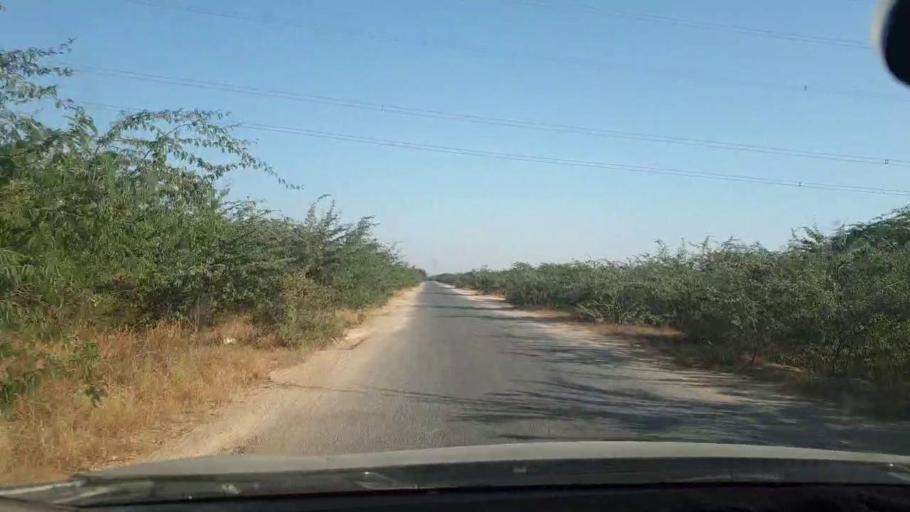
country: PK
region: Sindh
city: Malir Cantonment
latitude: 25.1616
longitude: 67.1946
